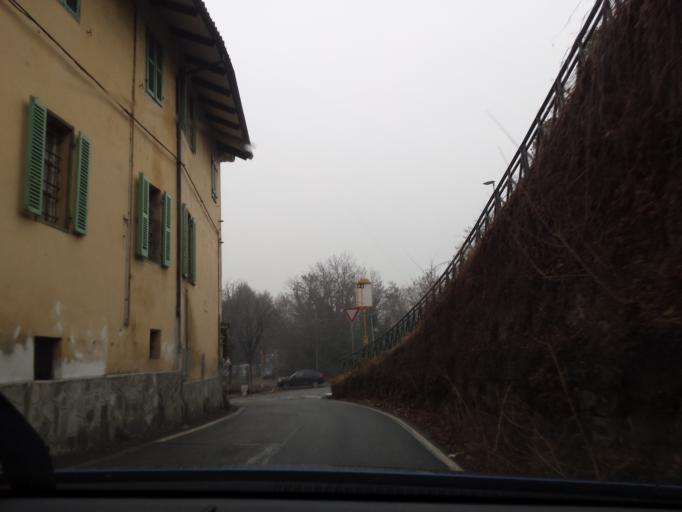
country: IT
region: Piedmont
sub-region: Provincia di Torino
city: Turin
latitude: 45.0521
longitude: 7.7185
